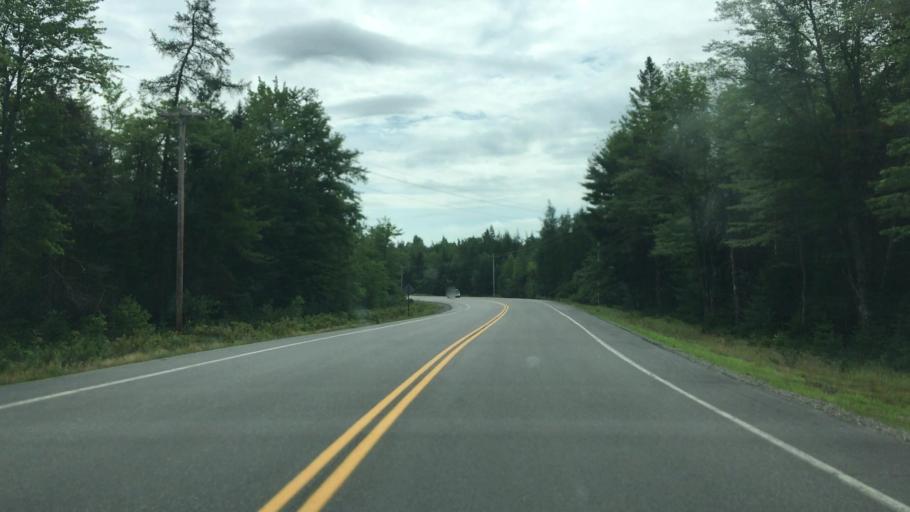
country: US
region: Maine
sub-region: Washington County
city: Machias
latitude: 44.9997
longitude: -67.5696
